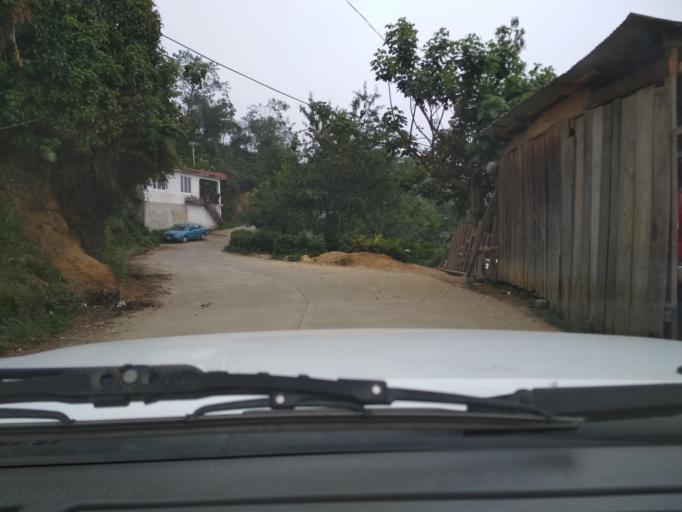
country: MX
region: Veracruz
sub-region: La Perla
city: Metlac Hernandez (Metlac Primero)
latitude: 18.9707
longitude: -97.1582
